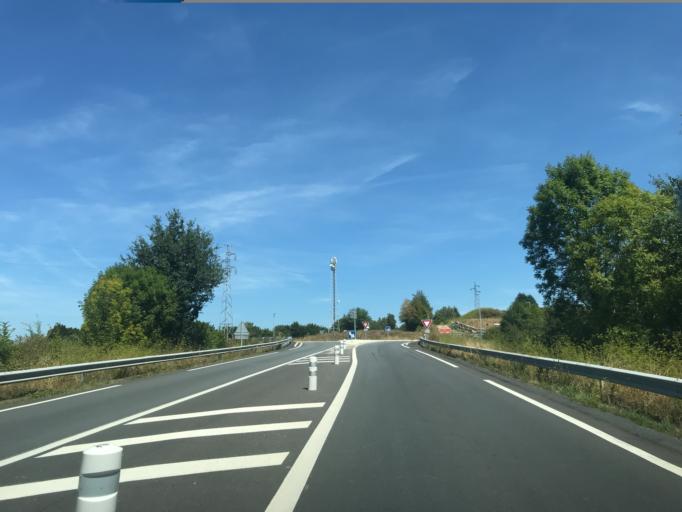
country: FR
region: Limousin
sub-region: Departement de la Correze
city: Tulle
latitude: 45.2827
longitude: 1.7976
